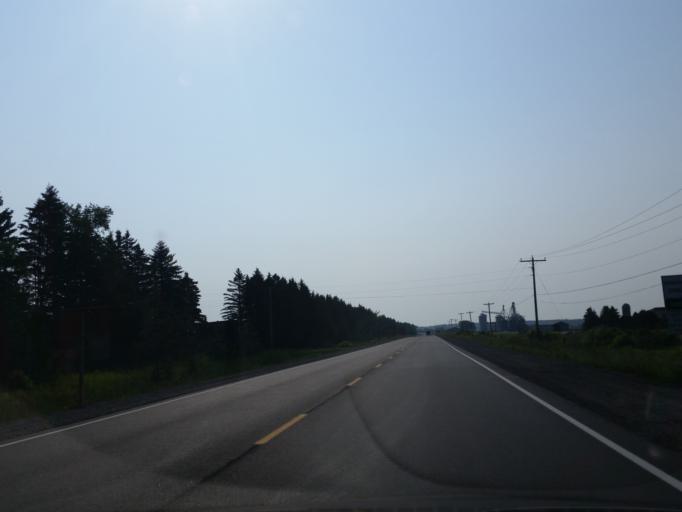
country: CA
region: Ontario
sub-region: Nipissing District
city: North Bay
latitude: 46.4108
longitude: -80.1152
